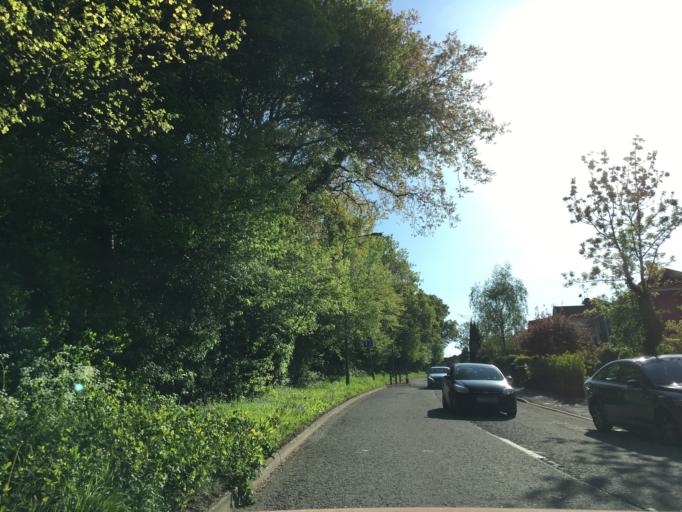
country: GB
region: Wales
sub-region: Cardiff
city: Cardiff
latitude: 51.5304
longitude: -3.1617
